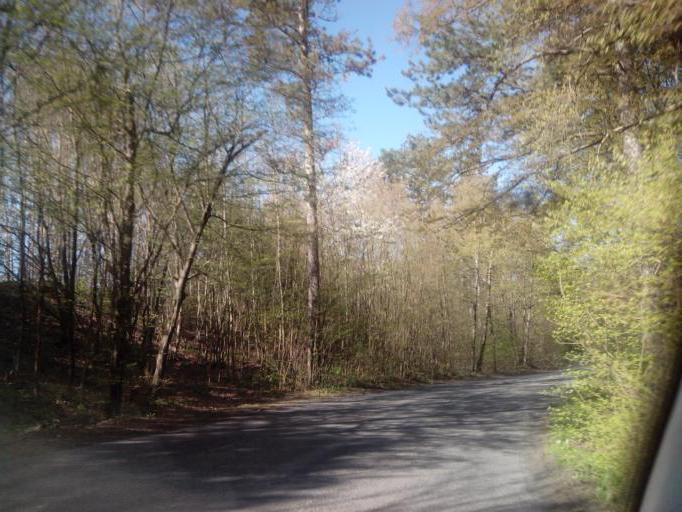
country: CZ
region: Central Bohemia
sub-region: Okres Beroun
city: Beroun
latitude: 49.9079
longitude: 14.0747
